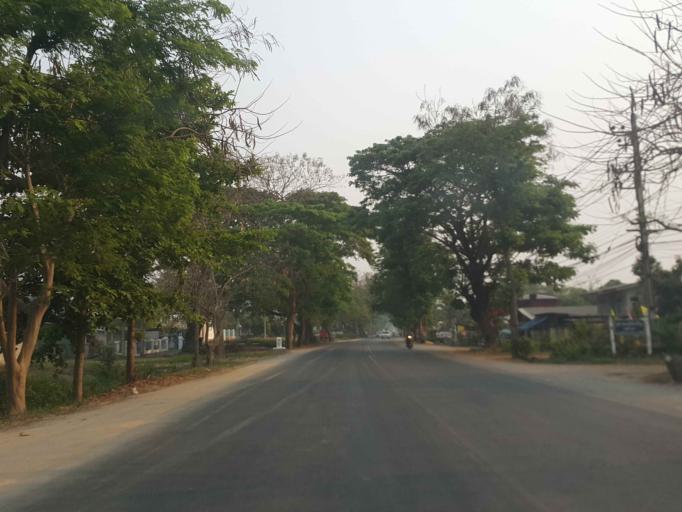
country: TH
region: Chiang Mai
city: San Sai
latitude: 18.9661
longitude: 98.9837
